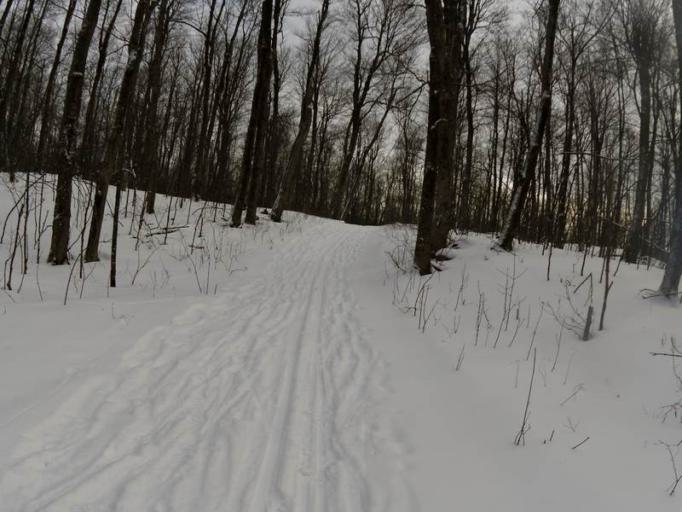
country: CA
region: Quebec
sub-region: Outaouais
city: Wakefield
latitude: 45.5232
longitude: -75.9139
